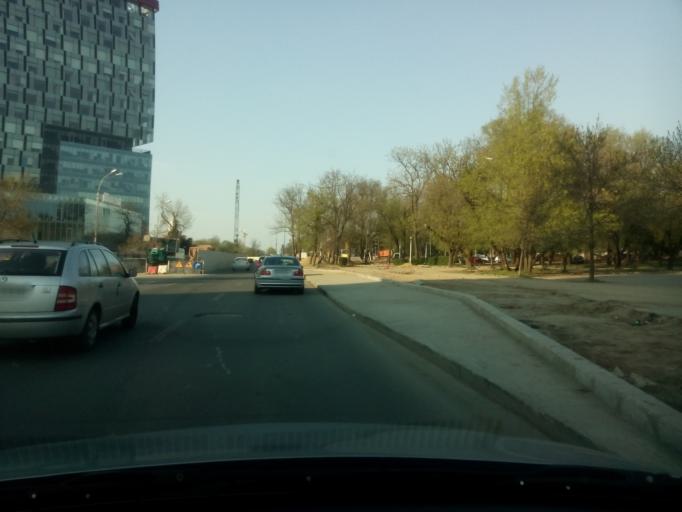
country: RO
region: Bucuresti
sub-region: Municipiul Bucuresti
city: Bucuresti
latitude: 44.4760
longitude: 26.0714
